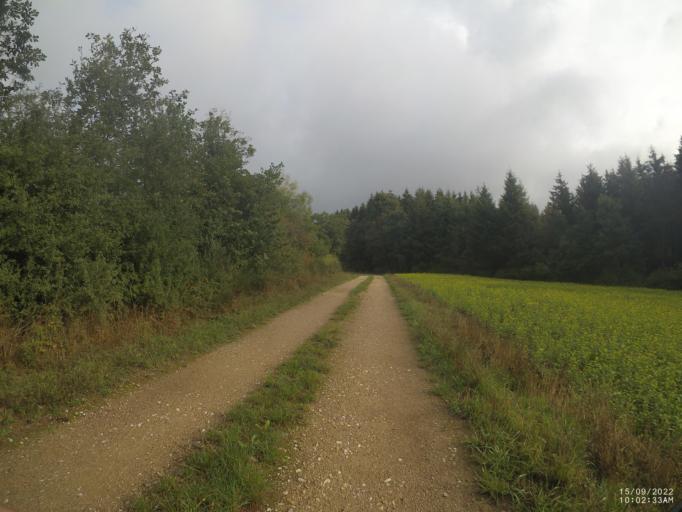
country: DE
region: Rheinland-Pfalz
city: Hoffeld
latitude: 50.3586
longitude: 6.8080
